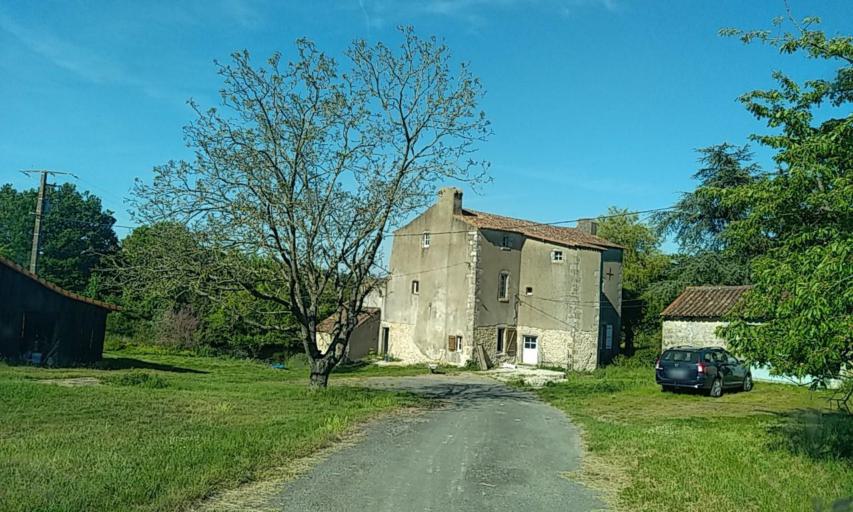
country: FR
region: Poitou-Charentes
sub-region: Departement des Deux-Sevres
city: Boisme
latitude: 46.7954
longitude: -0.4276
